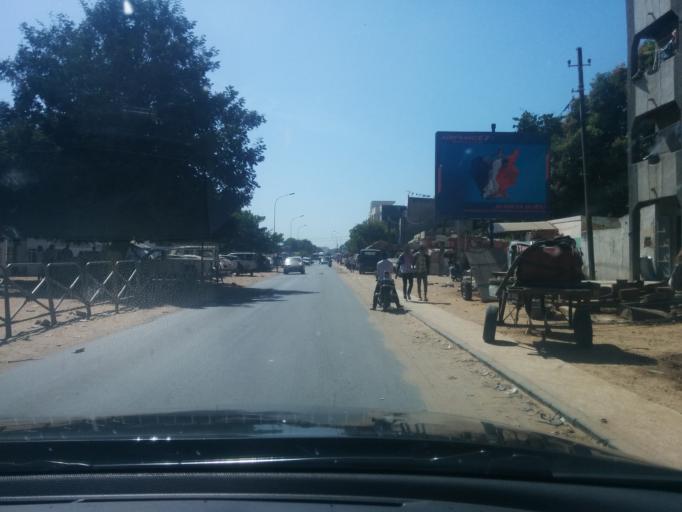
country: SN
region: Dakar
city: Grand Dakar
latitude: 14.7342
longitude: -17.4462
